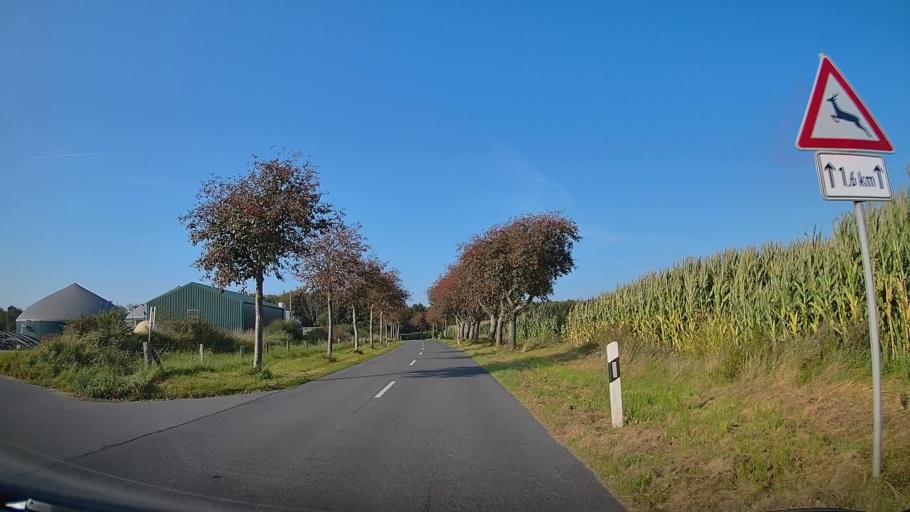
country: DE
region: Lower Saxony
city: Nordholz
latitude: 53.8004
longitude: 8.6096
